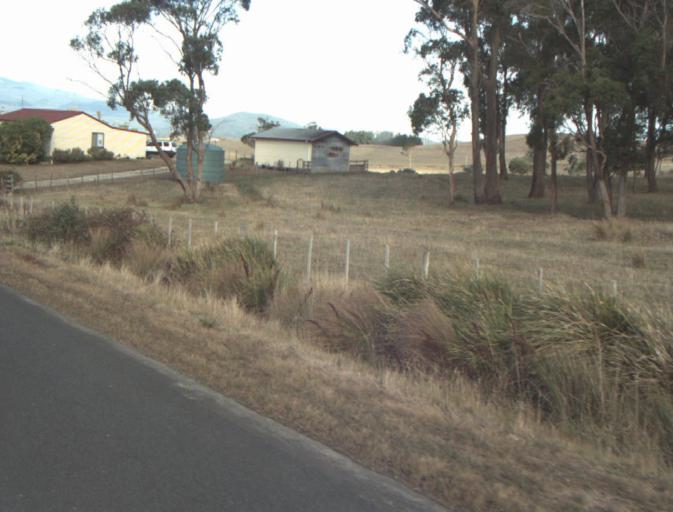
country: AU
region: Tasmania
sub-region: Launceston
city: Mayfield
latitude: -41.2083
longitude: 147.1044
